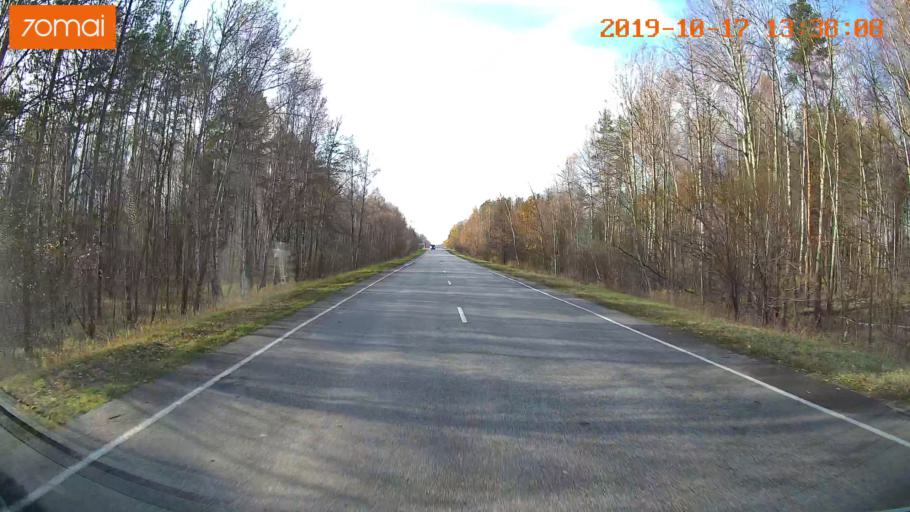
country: RU
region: Rjazan
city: Tuma
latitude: 55.1432
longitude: 40.6213
